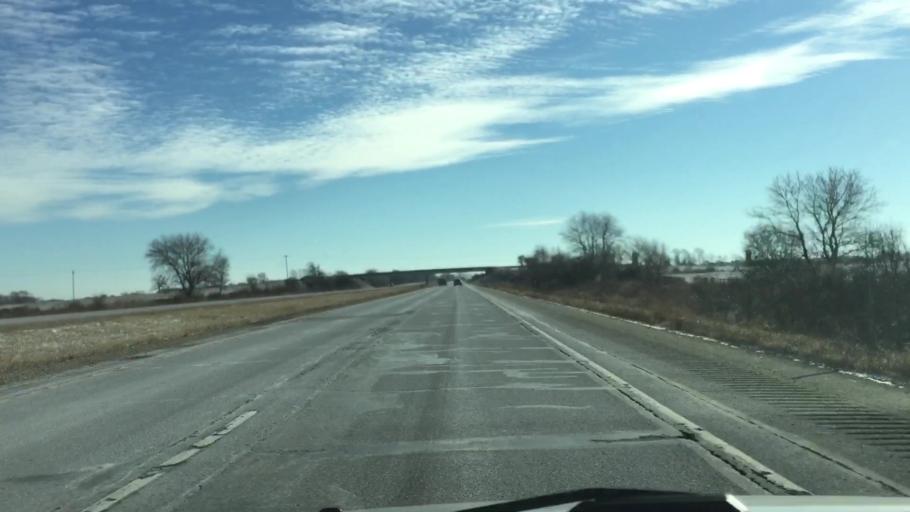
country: US
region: Wisconsin
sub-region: Walworth County
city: Como
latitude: 42.6405
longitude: -88.4912
